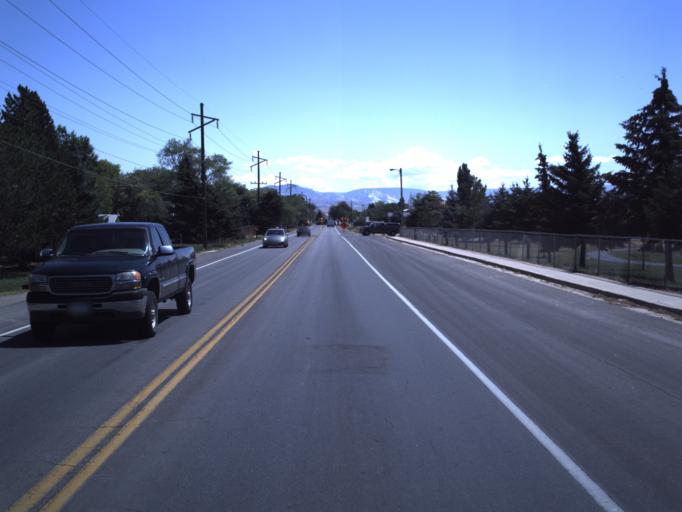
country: US
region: Utah
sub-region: Uintah County
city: Vernal
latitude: 40.4628
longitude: -109.5445
